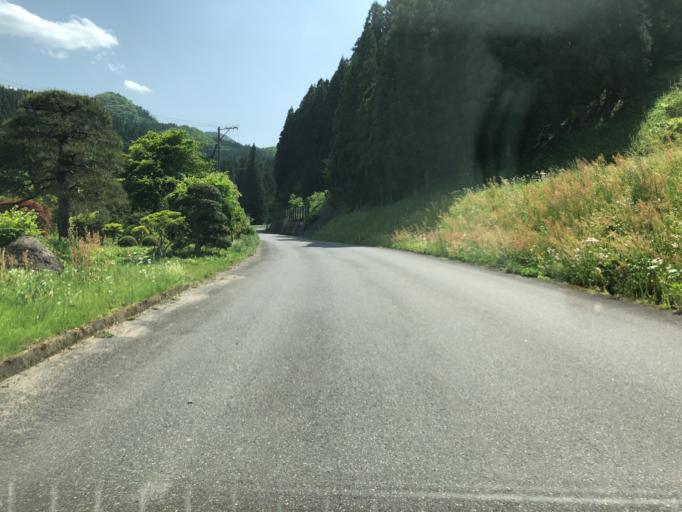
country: JP
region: Fukushima
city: Ishikawa
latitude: 37.0507
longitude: 140.5779
